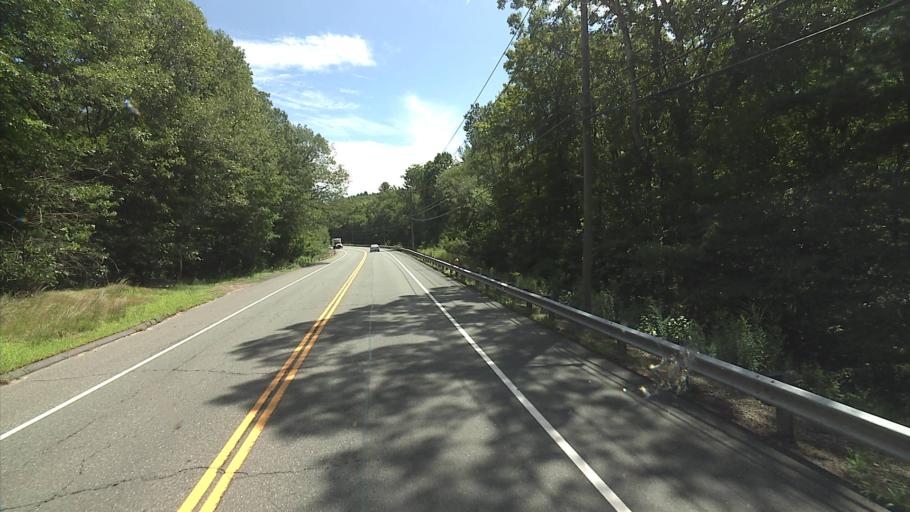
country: US
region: Connecticut
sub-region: Tolland County
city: Storrs
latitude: 41.8338
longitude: -72.3043
